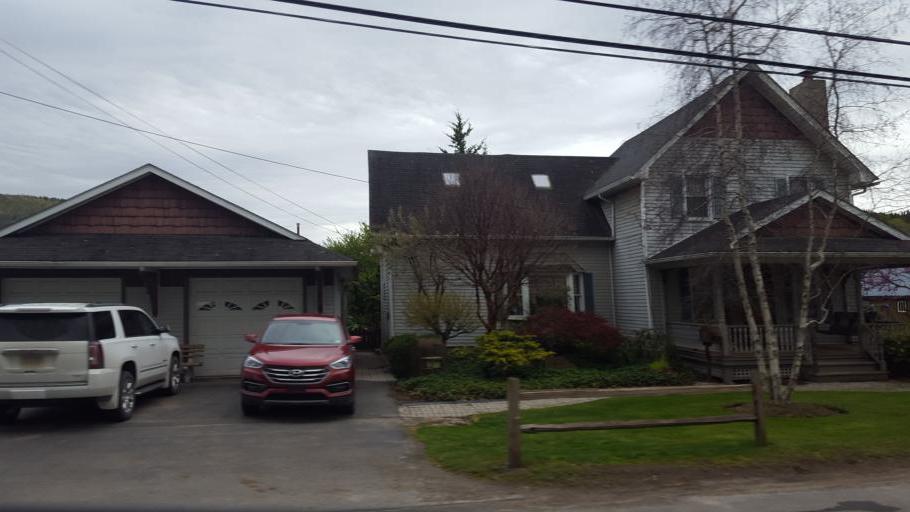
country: US
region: Pennsylvania
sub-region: Tioga County
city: Westfield
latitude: 41.9237
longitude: -77.5276
